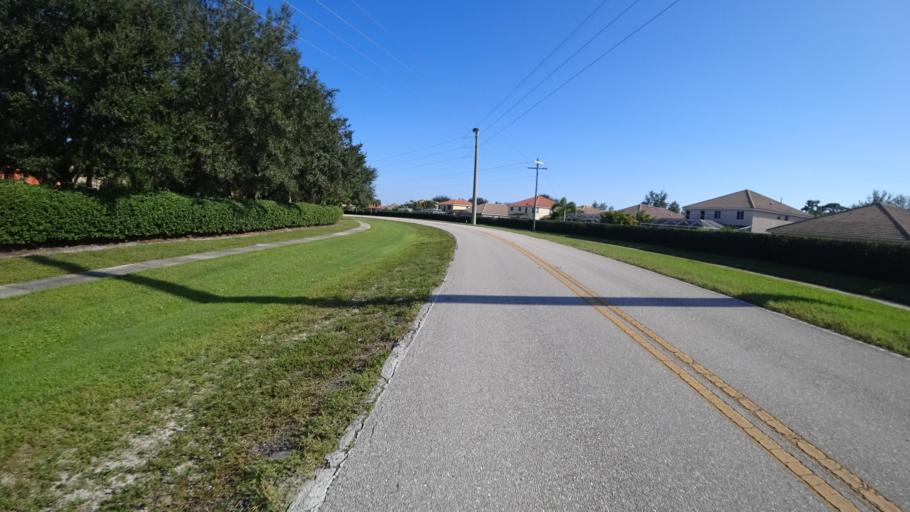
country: US
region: Florida
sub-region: Sarasota County
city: Desoto Lakes
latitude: 27.4184
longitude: -82.4628
